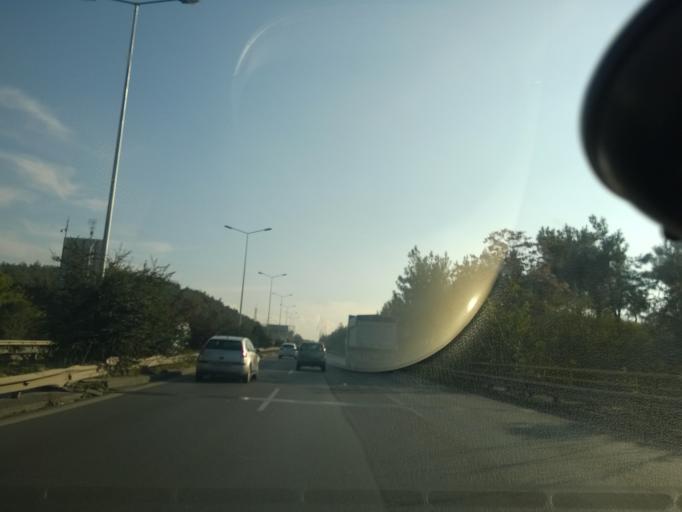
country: GR
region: Central Macedonia
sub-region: Nomos Thessalonikis
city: Agios Pavlos
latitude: 40.6494
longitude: 22.9670
